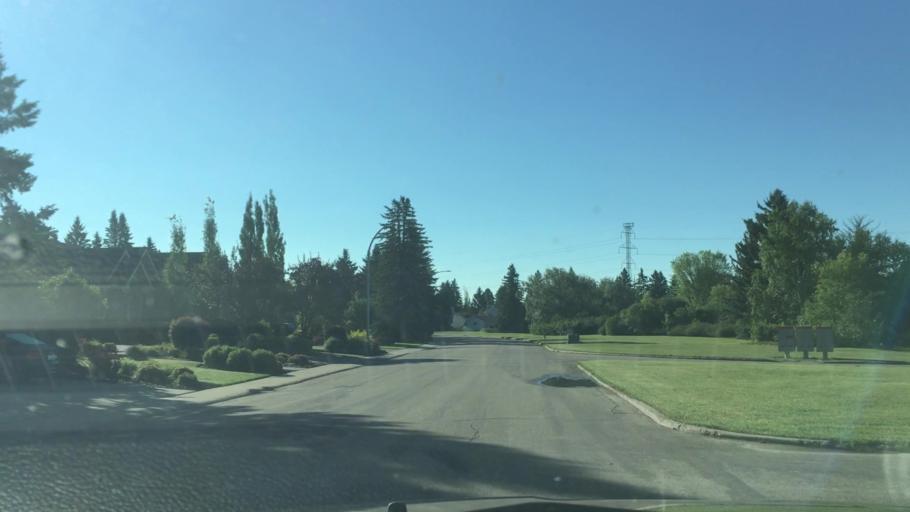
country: CA
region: Alberta
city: Edmonton
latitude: 53.4639
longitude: -113.5452
